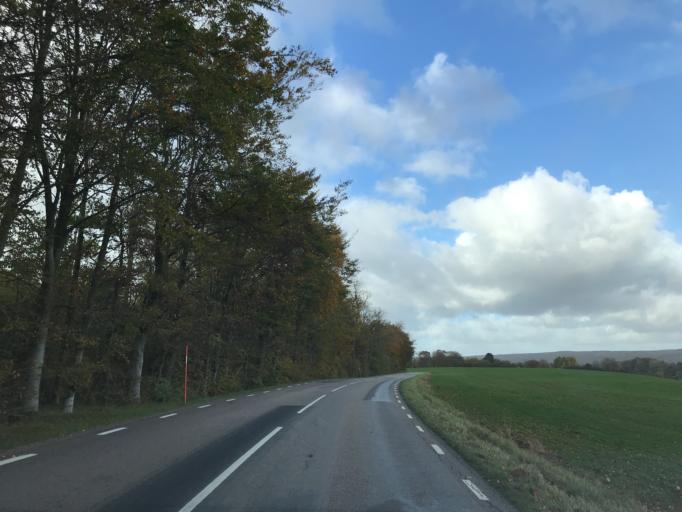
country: SE
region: Skane
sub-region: Svalovs Kommun
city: Kagerod
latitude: 56.0218
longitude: 13.0472
